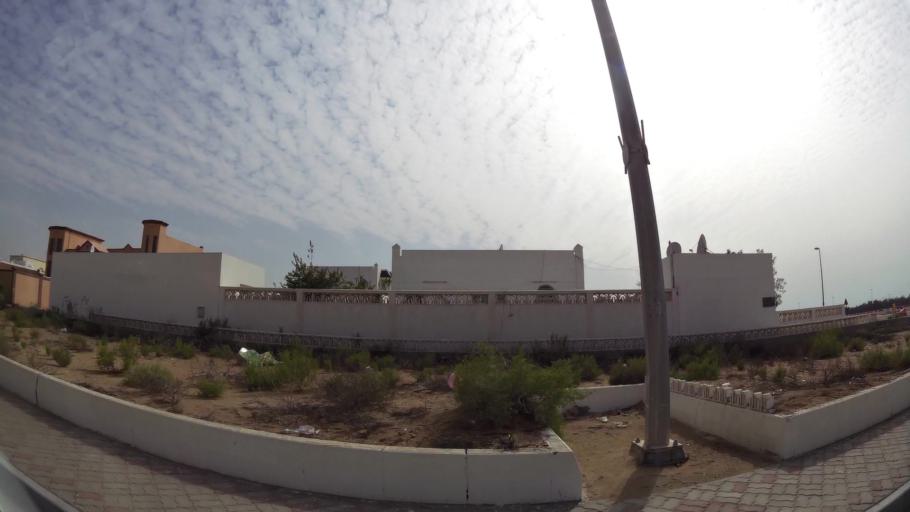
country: AE
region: Abu Dhabi
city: Abu Dhabi
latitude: 24.6156
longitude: 54.7039
